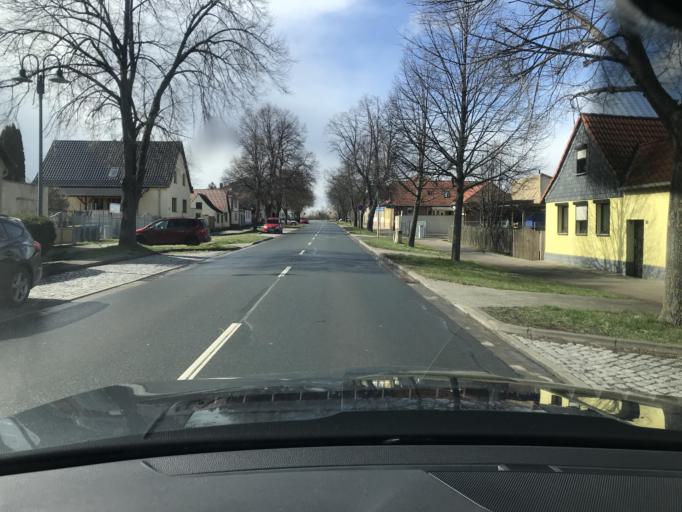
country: DE
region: Saxony-Anhalt
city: Hoym
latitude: 51.7830
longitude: 11.3082
